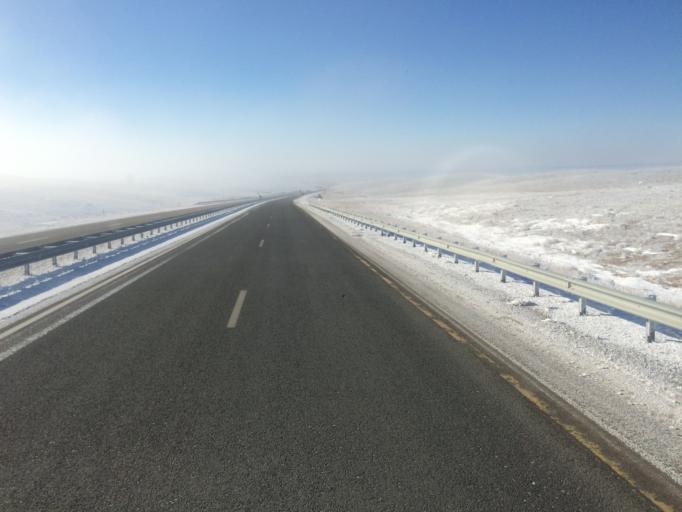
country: KZ
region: Zhambyl
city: Georgiyevka
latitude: 43.3922
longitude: 74.8120
